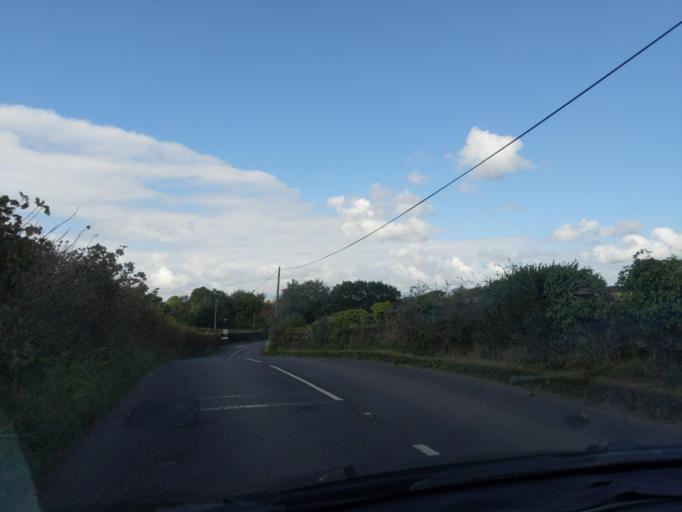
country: GB
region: England
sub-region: Cornwall
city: Boyton
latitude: 50.7115
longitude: -4.3297
